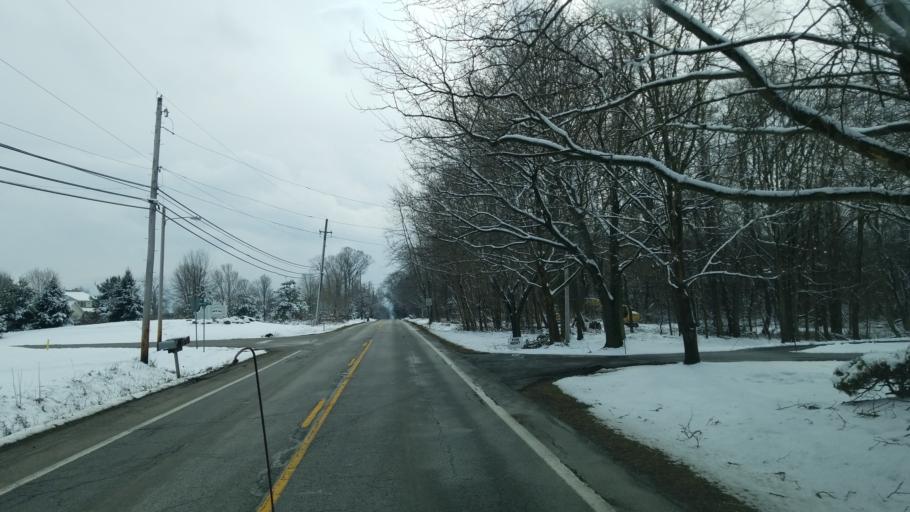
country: US
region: Ohio
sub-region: Portage County
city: Hiram
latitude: 41.3811
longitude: -81.1431
